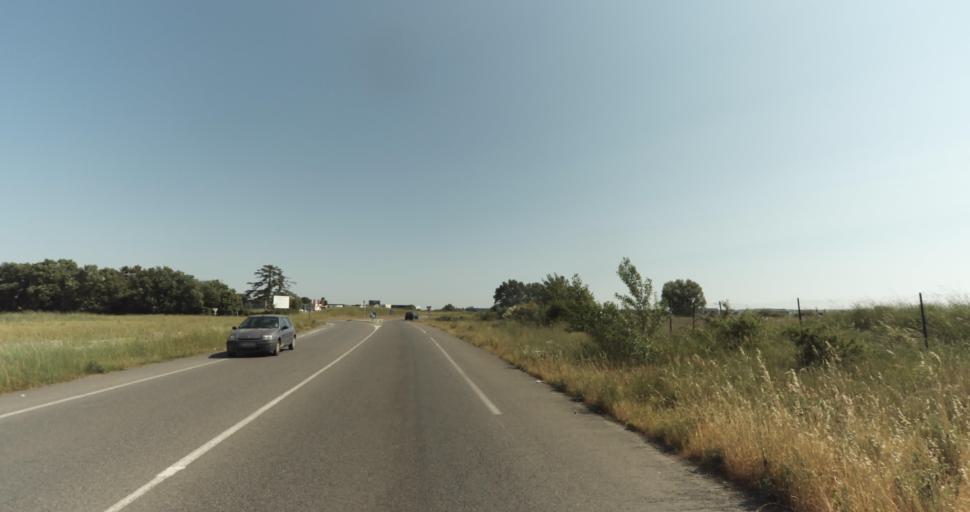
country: FR
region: Midi-Pyrenees
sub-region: Departement de la Haute-Garonne
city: La Salvetat-Saint-Gilles
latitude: 43.5915
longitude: 1.2849
